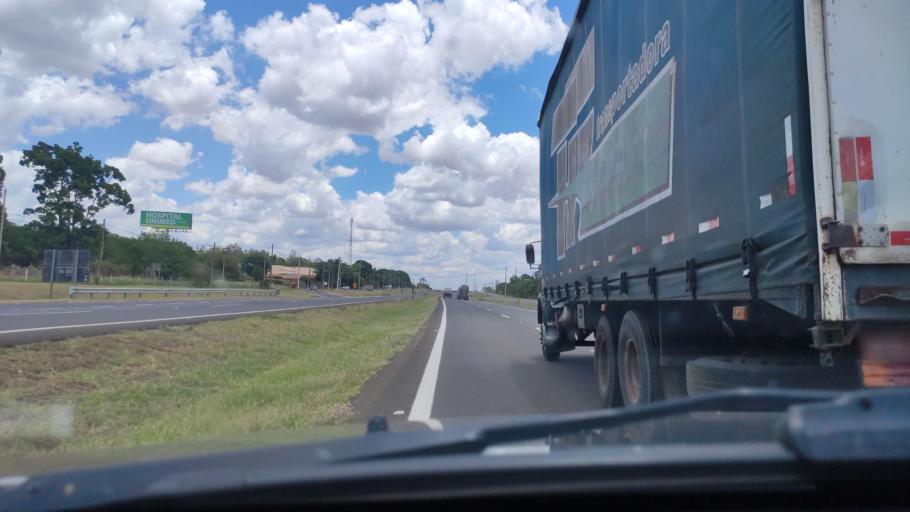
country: BR
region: Sao Paulo
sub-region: Bauru
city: Bauru
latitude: -22.3207
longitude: -48.9739
